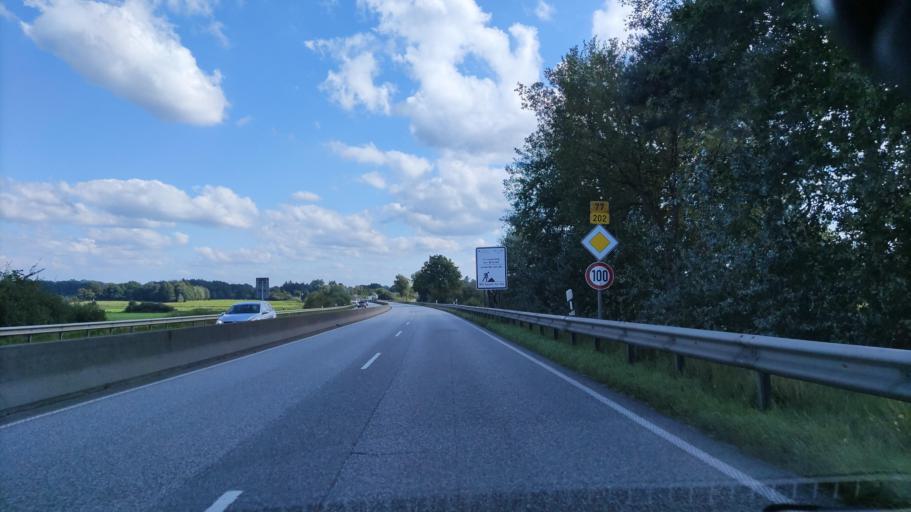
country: DE
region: Schleswig-Holstein
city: Westerronfeld
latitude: 54.3074
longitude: 9.6304
